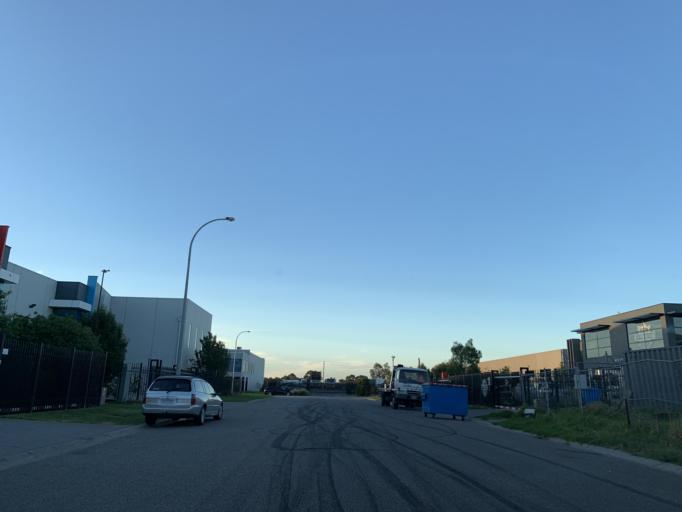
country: AU
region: Victoria
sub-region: Kingston
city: Aspendale Gardens
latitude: -38.0106
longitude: 145.1082
